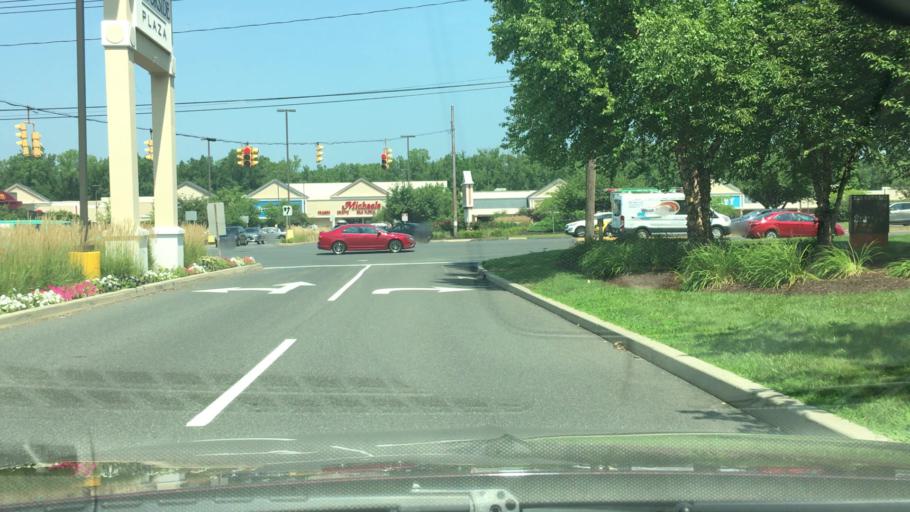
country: US
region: Connecticut
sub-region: Hartford County
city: Enfield
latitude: 41.9895
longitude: -72.5816
